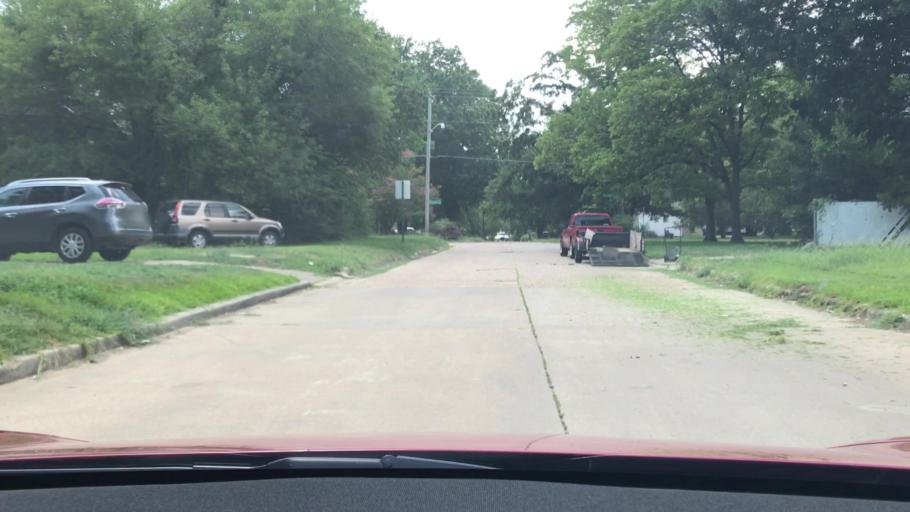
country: US
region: Louisiana
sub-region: Bossier Parish
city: Bossier City
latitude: 32.4963
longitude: -93.7282
